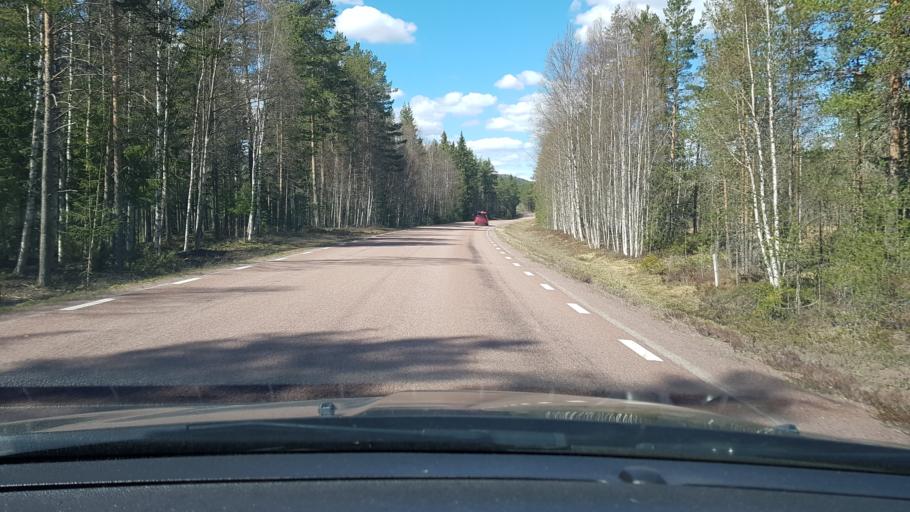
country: SE
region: Dalarna
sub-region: Alvdalens Kommun
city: AElvdalen
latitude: 61.1252
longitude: 14.0319
